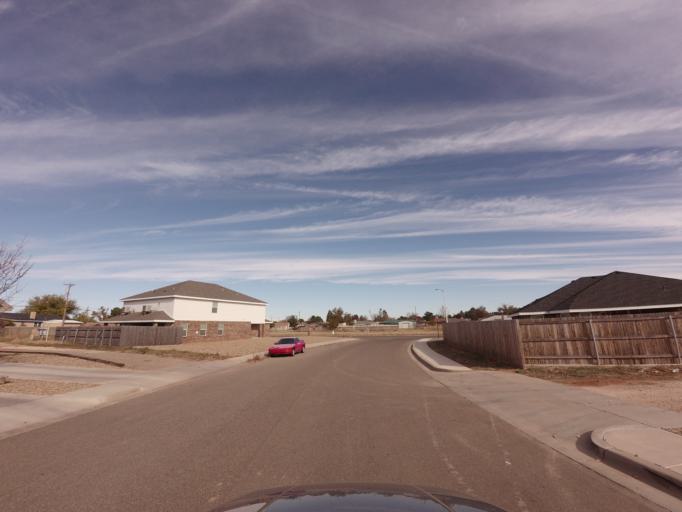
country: US
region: New Mexico
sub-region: Curry County
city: Clovis
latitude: 34.4221
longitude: -103.2225
